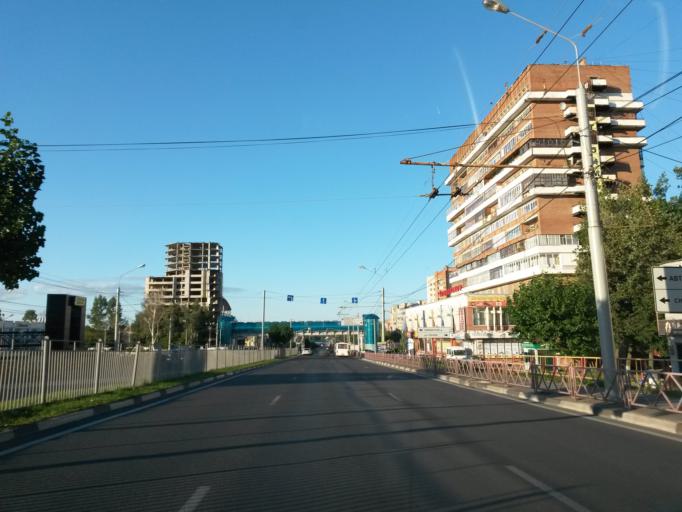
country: RU
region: Jaroslavl
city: Yaroslavl
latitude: 57.5917
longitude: 39.8619
